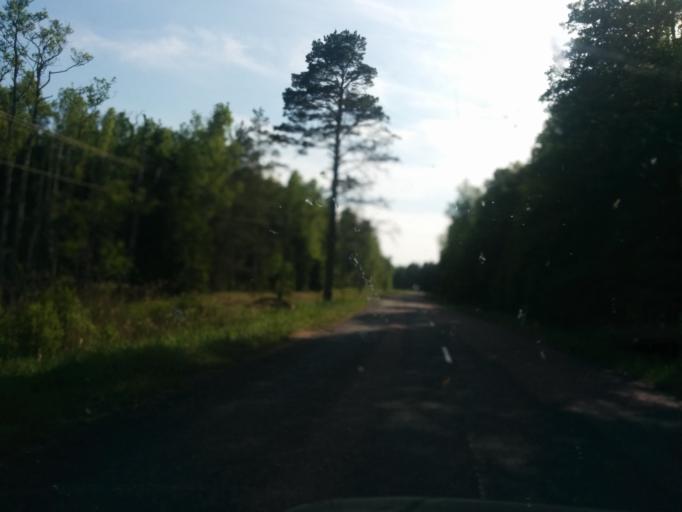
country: LV
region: Dundaga
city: Dundaga
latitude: 57.6558
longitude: 22.2751
